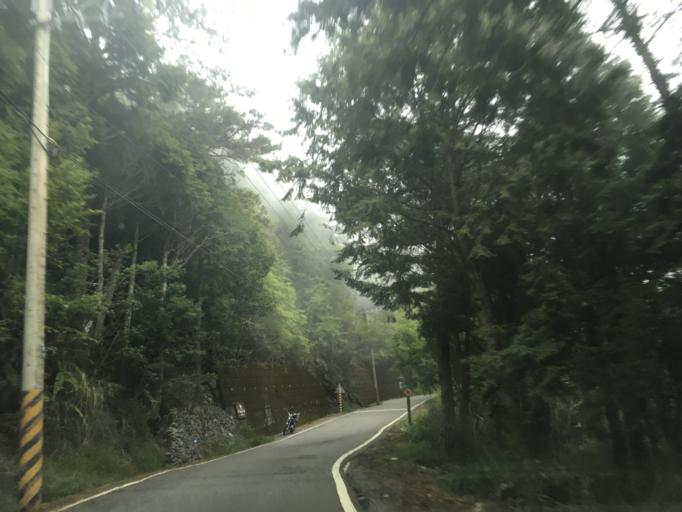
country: TW
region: Taiwan
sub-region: Nantou
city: Puli
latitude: 24.2553
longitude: 121.0092
